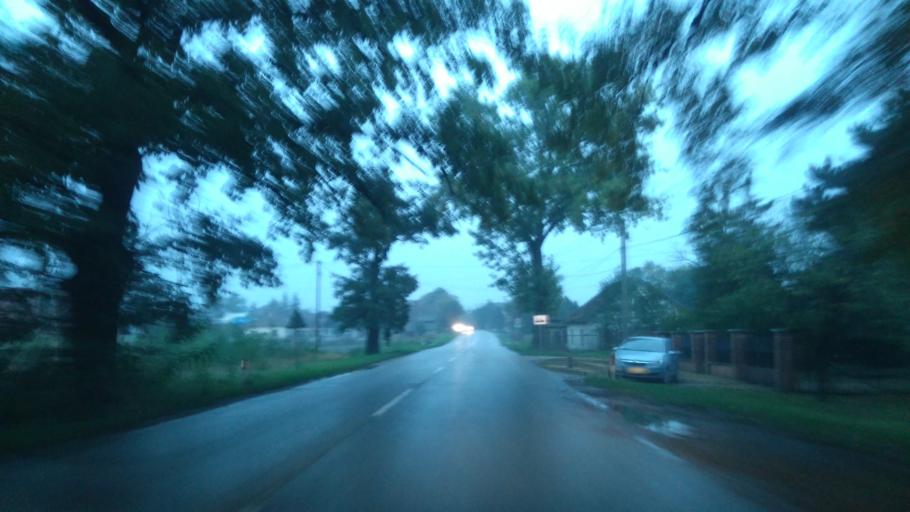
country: RS
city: Backo Petrovo Selo
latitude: 45.6930
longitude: 20.0804
